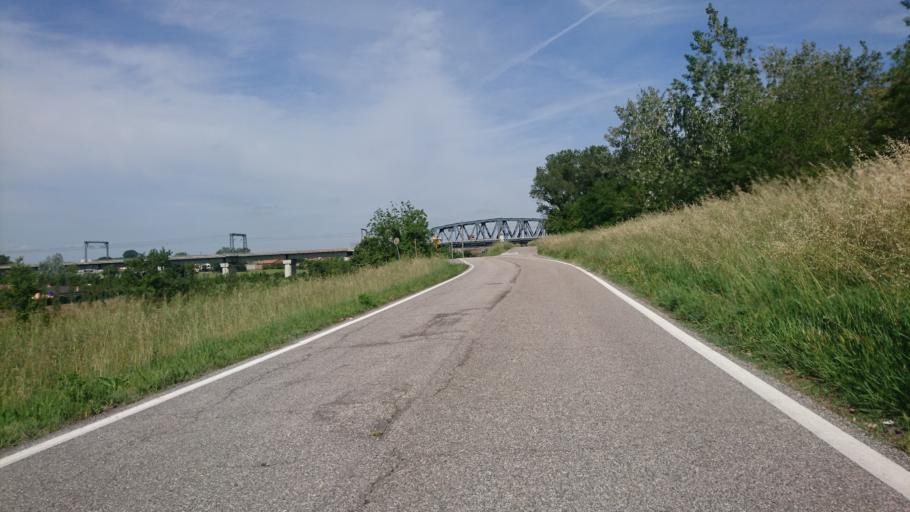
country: IT
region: Lombardy
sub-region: Provincia di Mantova
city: Revere
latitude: 45.0493
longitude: 11.1383
